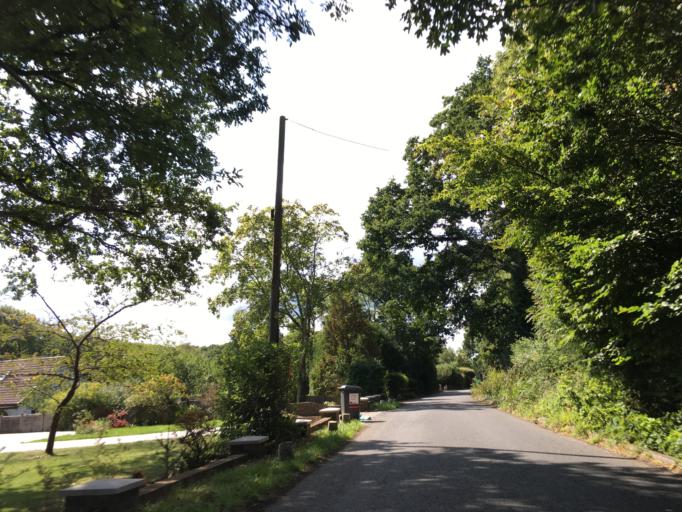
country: GB
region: England
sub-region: Hampshire
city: Colden Common
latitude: 50.9897
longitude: -1.3009
